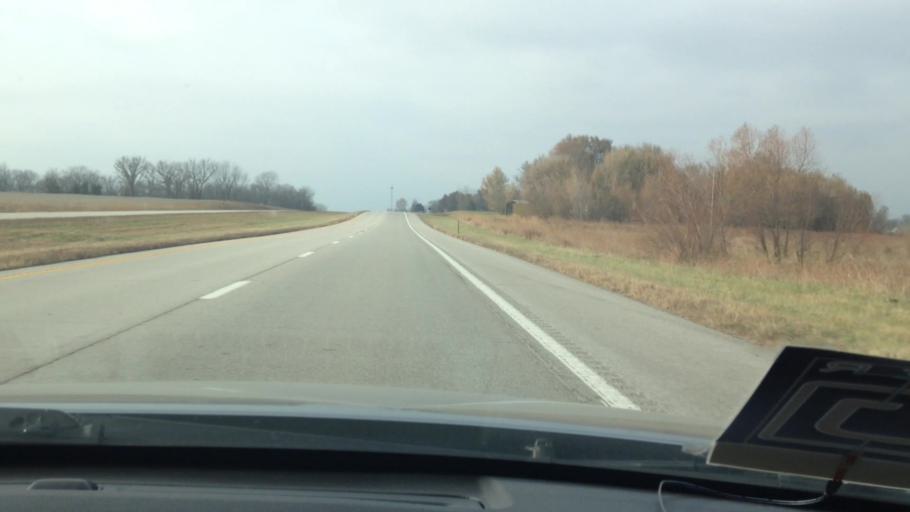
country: US
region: Missouri
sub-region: Cass County
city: Garden City
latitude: 38.5413
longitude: -94.1623
